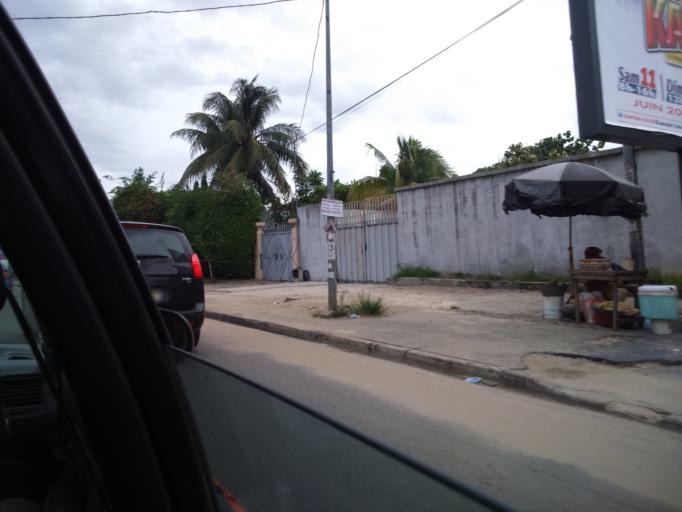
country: CI
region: Lagunes
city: Abidjan
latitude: 5.3573
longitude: -3.9913
